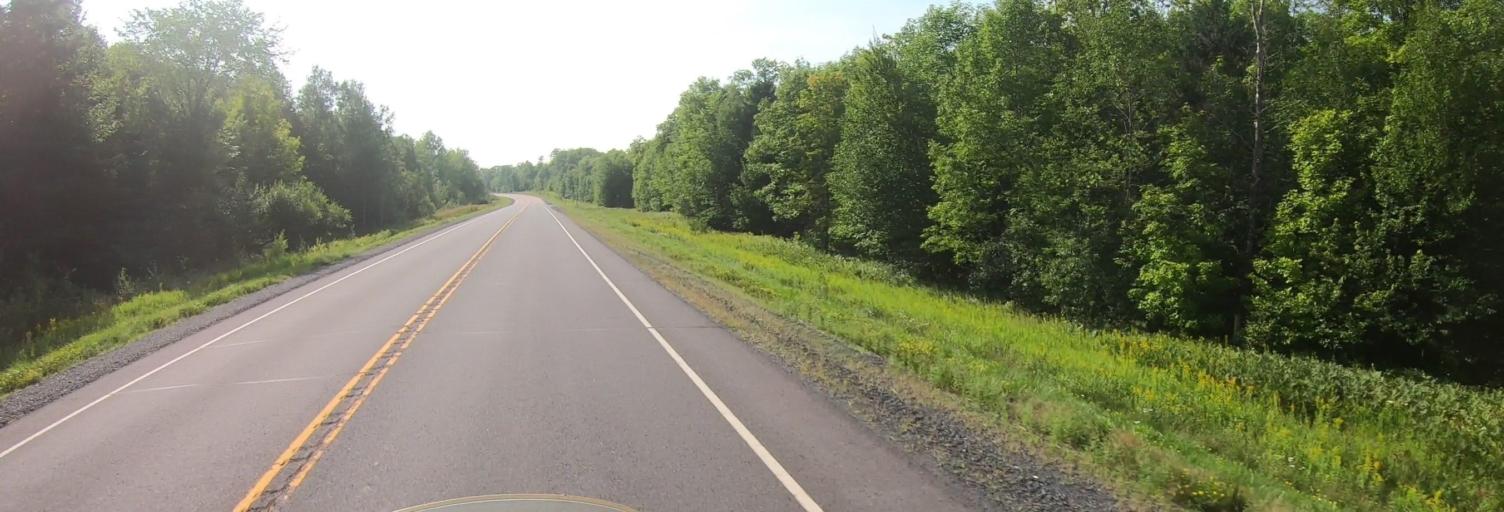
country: US
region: Wisconsin
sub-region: Iron County
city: Hurley
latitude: 46.3671
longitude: -90.4170
